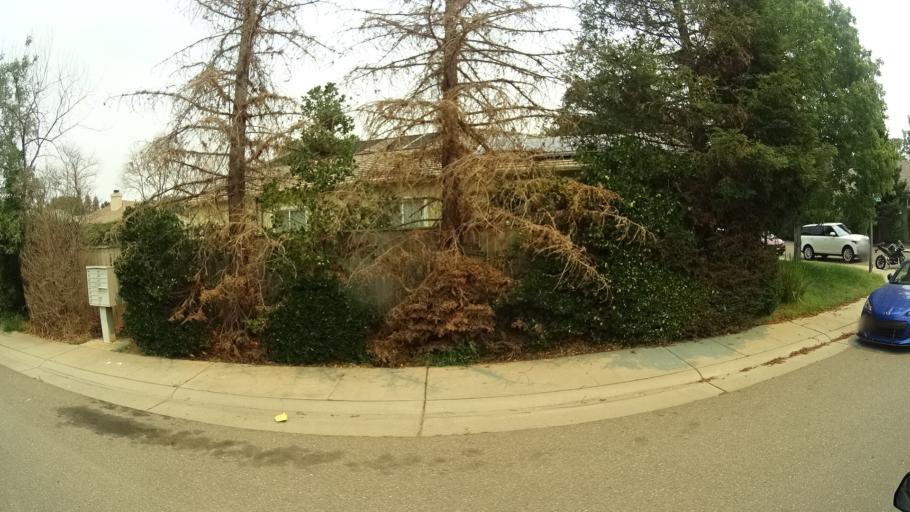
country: US
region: California
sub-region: Sacramento County
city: Laguna
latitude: 38.4005
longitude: -121.4190
